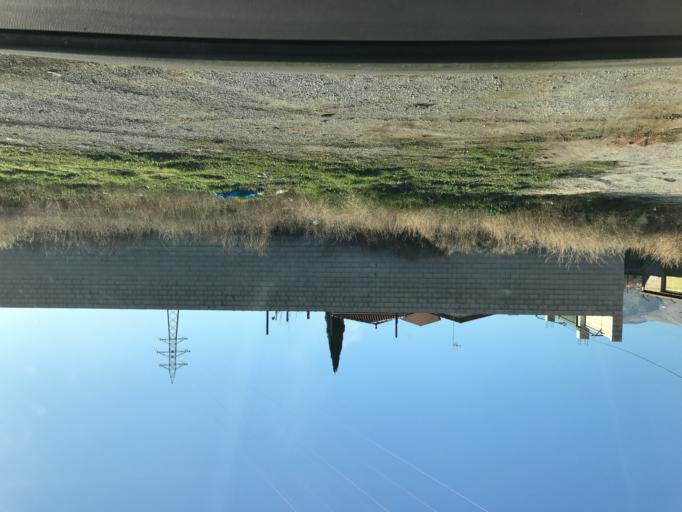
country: ES
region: Andalusia
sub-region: Provincia de Granada
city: Pulianas
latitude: 37.2164
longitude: -3.6022
